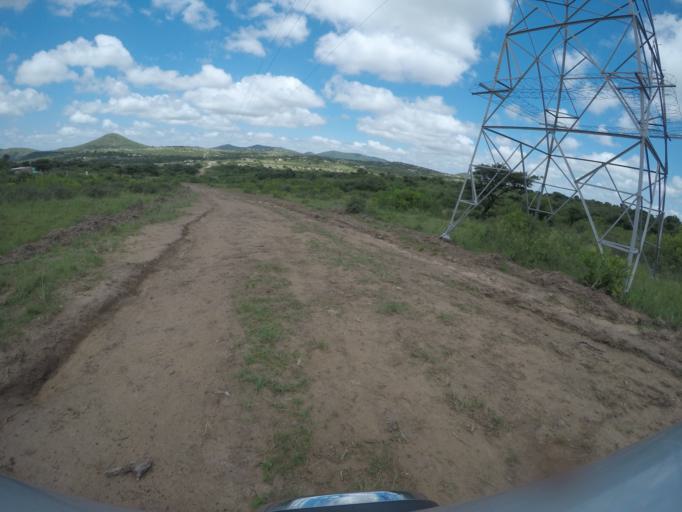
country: ZA
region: KwaZulu-Natal
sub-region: uThungulu District Municipality
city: Empangeni
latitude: -28.5865
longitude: 31.8359
